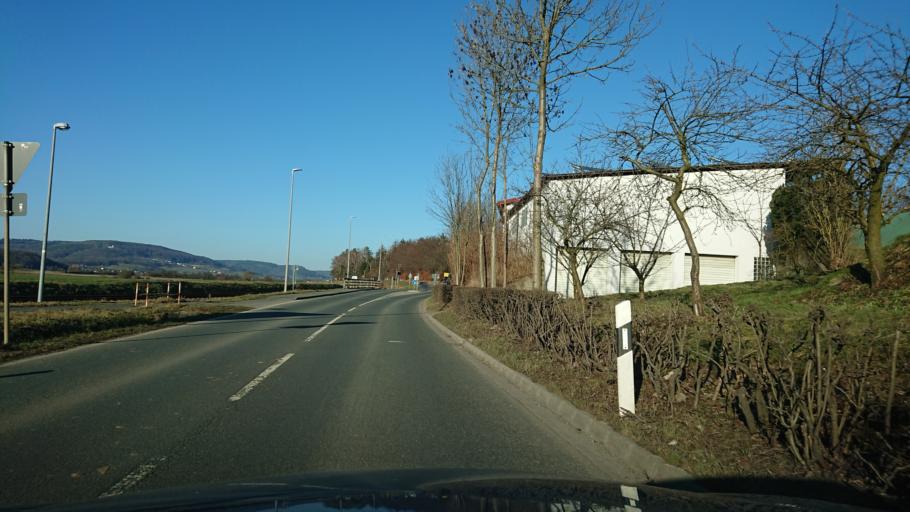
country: DE
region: Bavaria
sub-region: Upper Franconia
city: Wiesenthau
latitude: 49.7138
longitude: 11.1277
